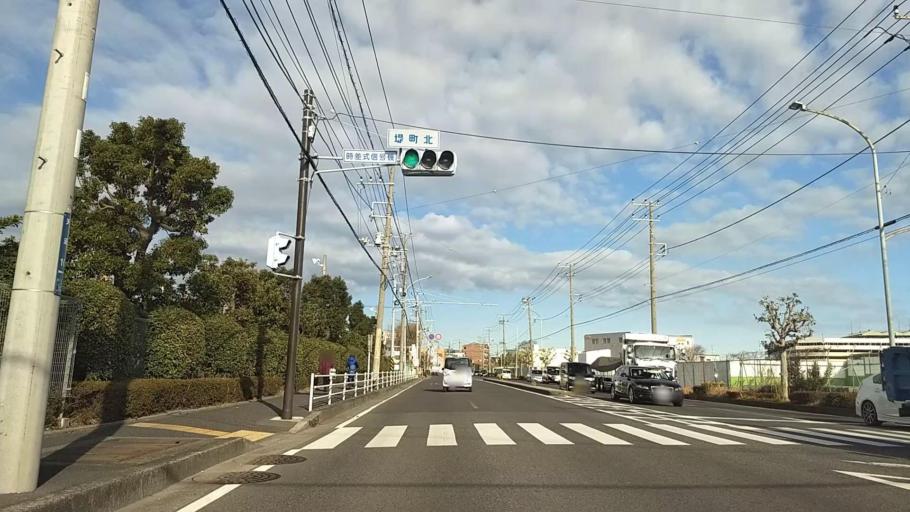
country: JP
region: Kanagawa
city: Hiratsuka
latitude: 35.3388
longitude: 139.3569
